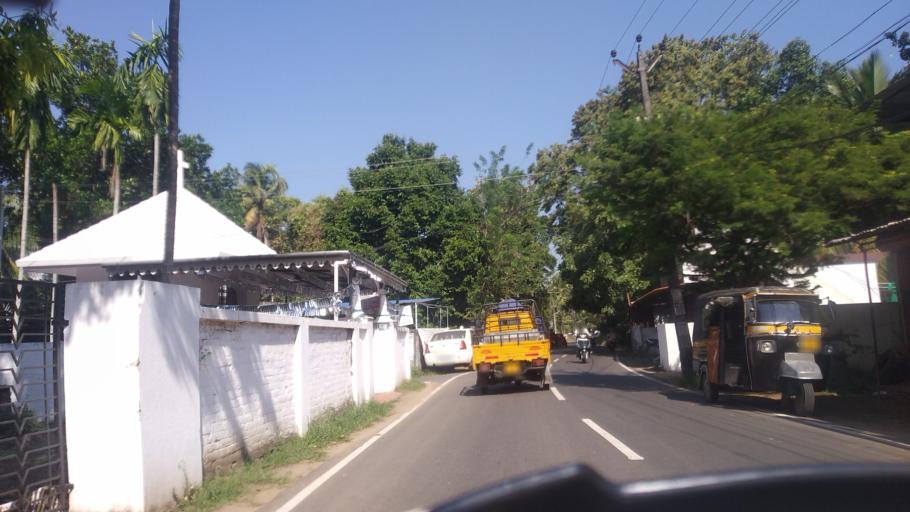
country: IN
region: Kerala
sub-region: Ernakulam
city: Elur
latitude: 10.1139
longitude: 76.2480
